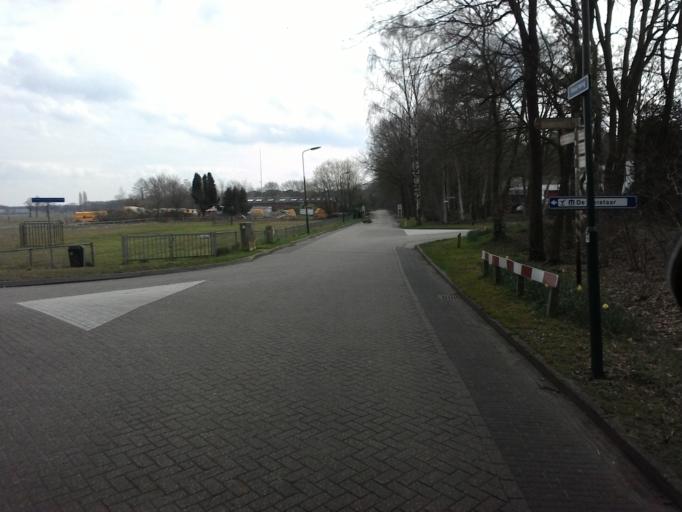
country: NL
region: Utrecht
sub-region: Gemeente Utrechtse Heuvelrug
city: Maarsbergen
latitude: 52.0568
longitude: 5.4135
